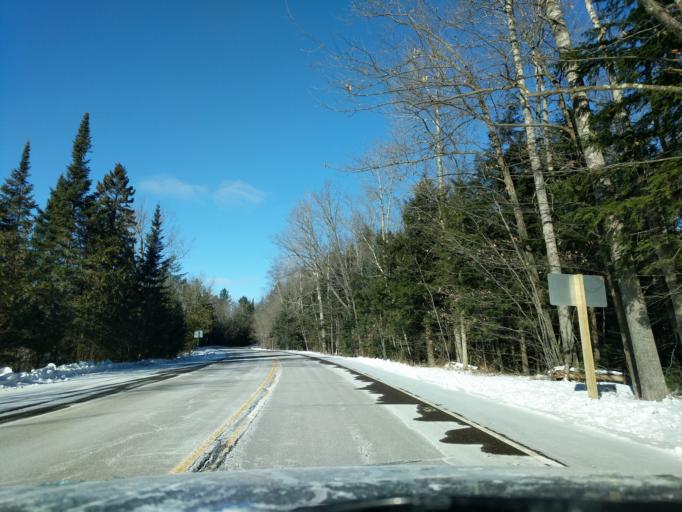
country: US
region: Wisconsin
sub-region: Menominee County
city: Keshena
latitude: 45.1071
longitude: -88.6384
